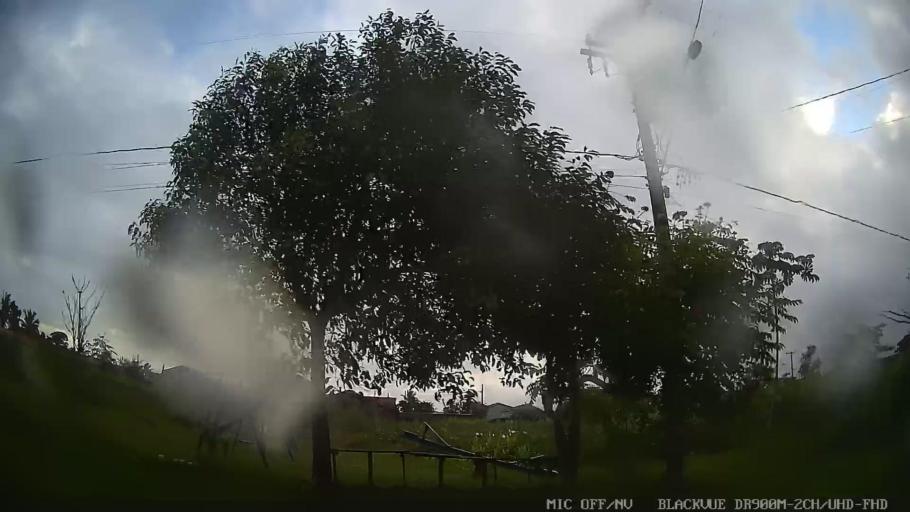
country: BR
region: Sao Paulo
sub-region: Itanhaem
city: Itanhaem
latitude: -24.2055
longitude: -46.8389
